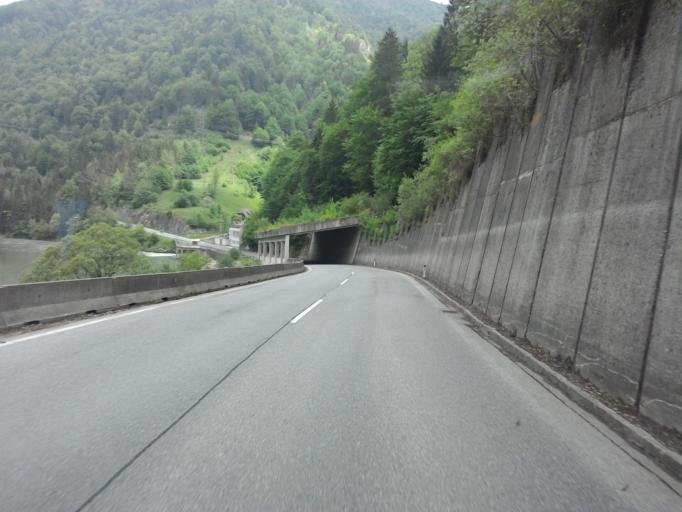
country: AT
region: Styria
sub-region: Politischer Bezirk Liezen
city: Altenmarkt bei Sankt Gallen
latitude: 47.7363
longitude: 14.6520
